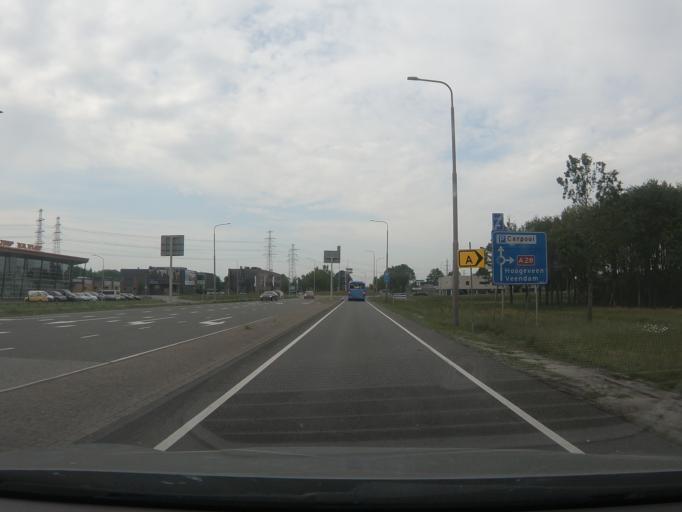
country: NL
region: Drenthe
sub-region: Gemeente Assen
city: Assen
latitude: 52.9937
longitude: 6.5219
